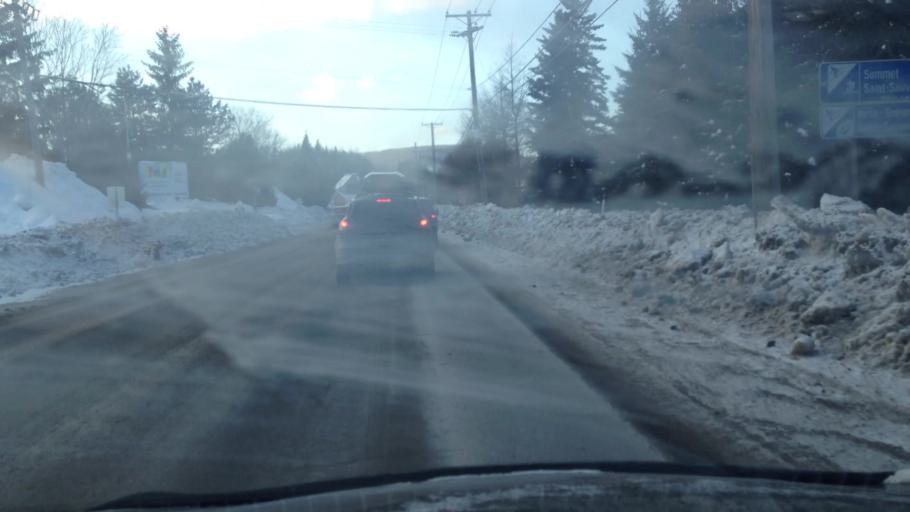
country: CA
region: Quebec
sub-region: Laurentides
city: Saint-Sauveur
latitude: 45.8864
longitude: -74.1328
